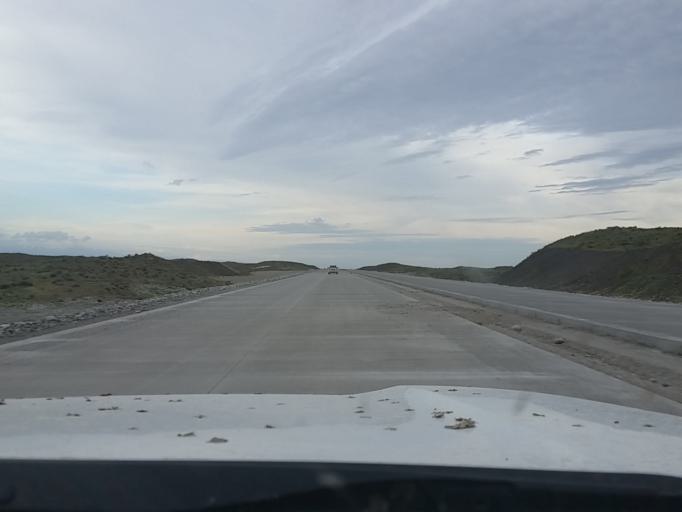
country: KZ
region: Almaty Oblysy
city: Zharkent
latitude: 44.1745
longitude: 80.3139
